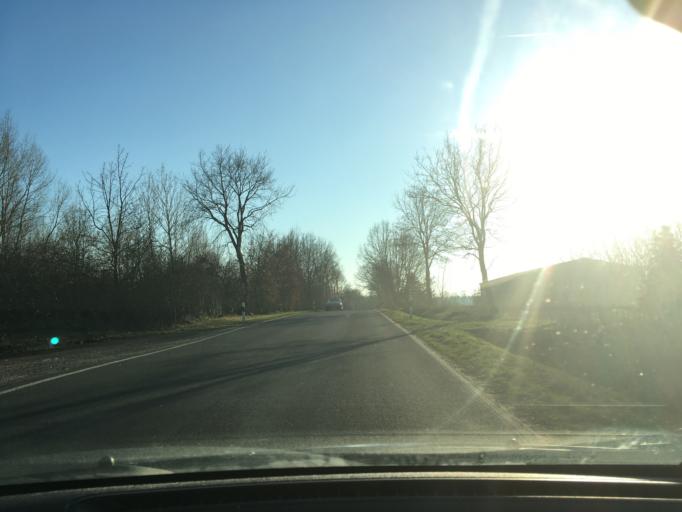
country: DE
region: Schleswig-Holstein
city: Mussen
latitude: 53.4939
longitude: 10.5548
